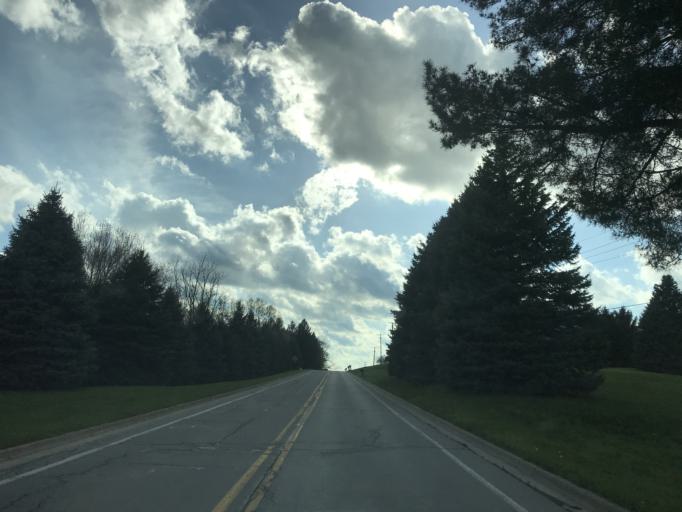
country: US
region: Michigan
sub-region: Livingston County
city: Brighton
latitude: 42.5457
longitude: -83.7319
